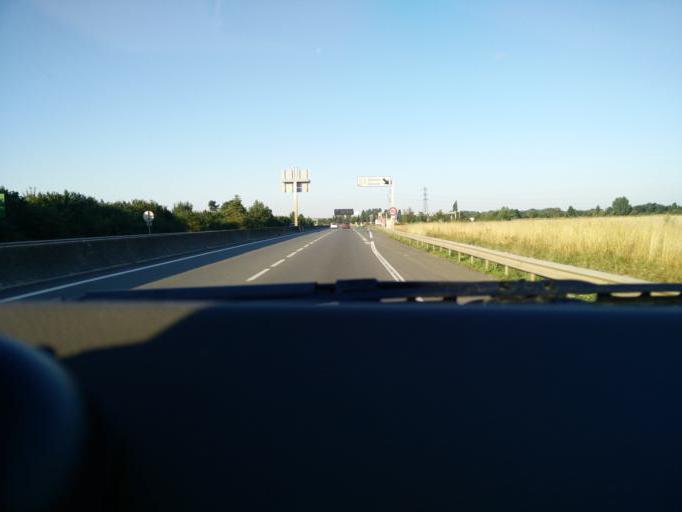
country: FR
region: Nord-Pas-de-Calais
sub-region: Departement du Nord
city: Santes
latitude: 50.6042
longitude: 2.9457
